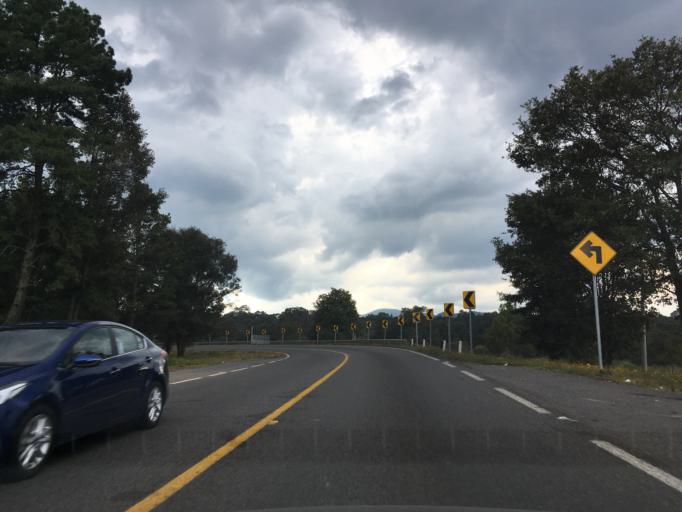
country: MX
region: Michoacan
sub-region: Patzcuaro
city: Santa Maria Huiramangaro (San Juan Tumbio)
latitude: 19.4974
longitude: -101.7134
